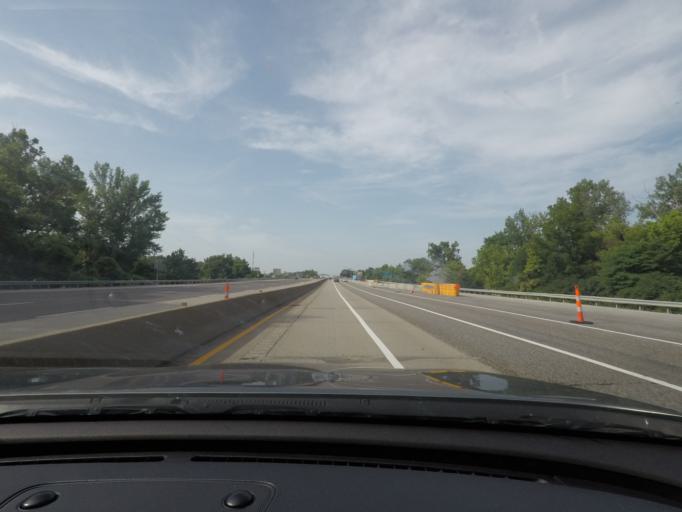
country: US
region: Missouri
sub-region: Saint Louis County
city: Maryland Heights
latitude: 38.7282
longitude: -90.4443
